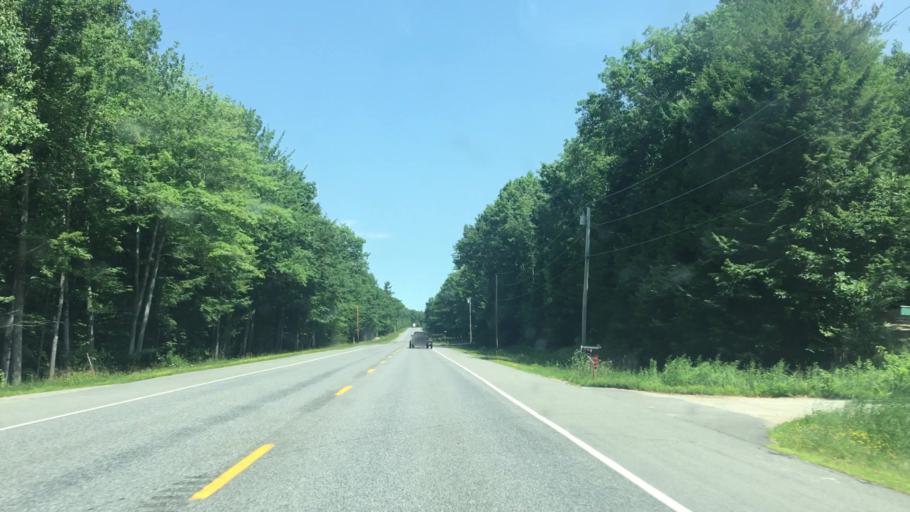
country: US
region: Maine
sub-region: Kennebec County
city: Monmouth
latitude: 44.2386
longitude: -70.0690
